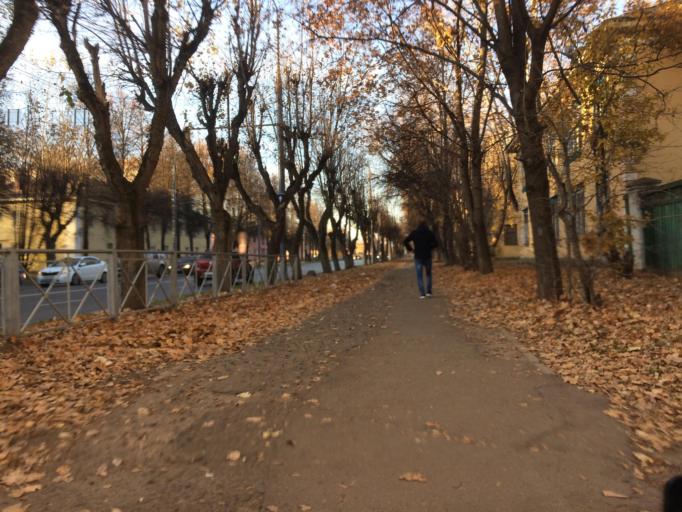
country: RU
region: Mariy-El
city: Yoshkar-Ola
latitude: 56.6378
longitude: 47.8667
